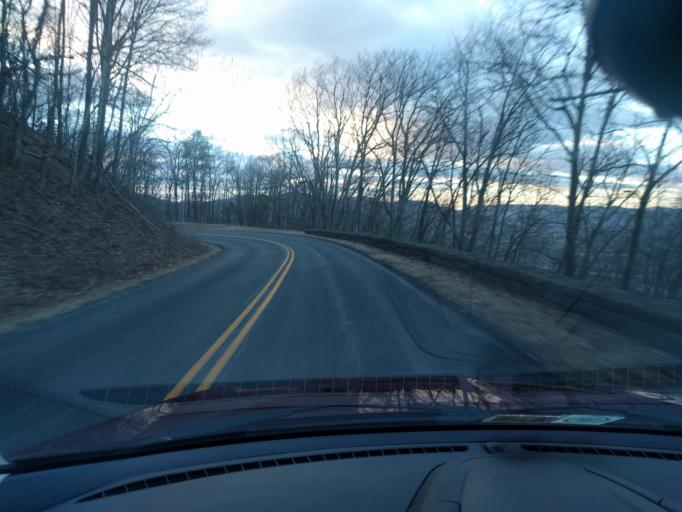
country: US
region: Virginia
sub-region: Botetourt County
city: Buchanan
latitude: 37.4786
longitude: -79.6534
